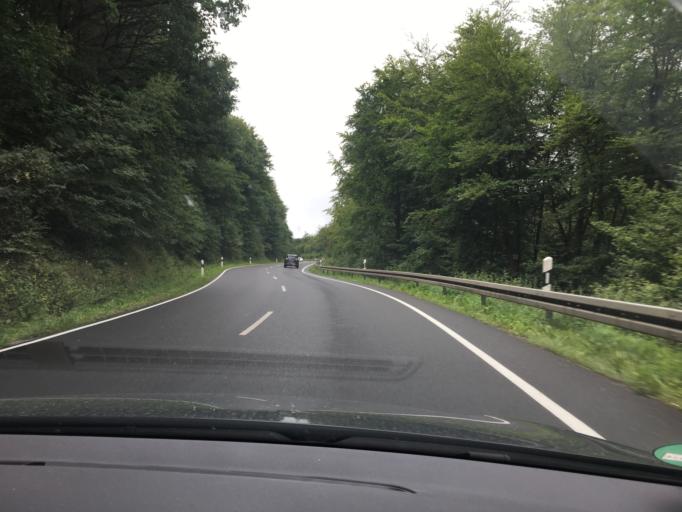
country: DE
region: North Rhine-Westphalia
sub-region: Regierungsbezirk Koln
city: Hurtgenwald
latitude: 50.7453
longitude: 6.4067
